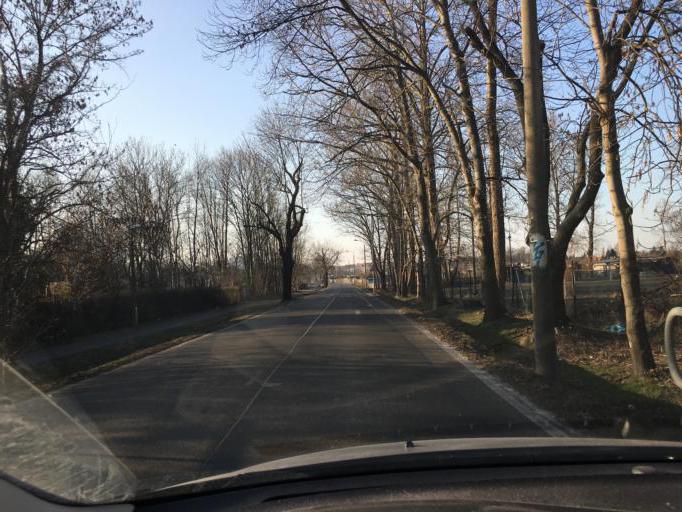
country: DE
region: Saxony
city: Leipzig
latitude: 51.3159
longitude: 12.4371
